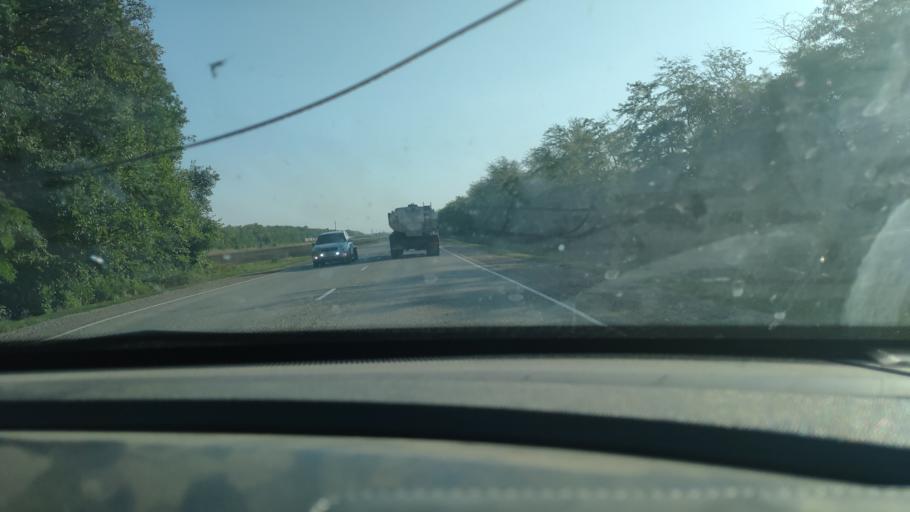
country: RU
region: Krasnodarskiy
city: Starominskaya
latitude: 46.4859
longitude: 39.0551
